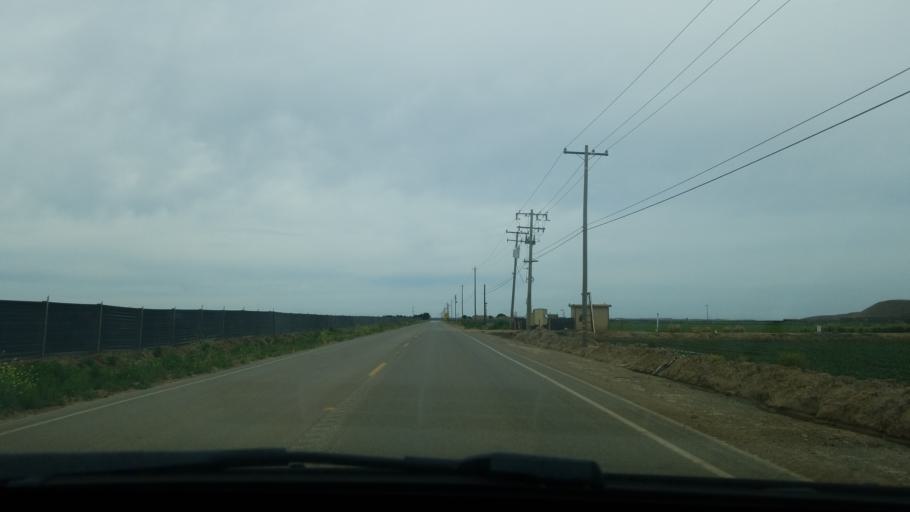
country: US
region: California
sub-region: San Luis Obispo County
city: Nipomo
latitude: 35.0047
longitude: -120.5127
